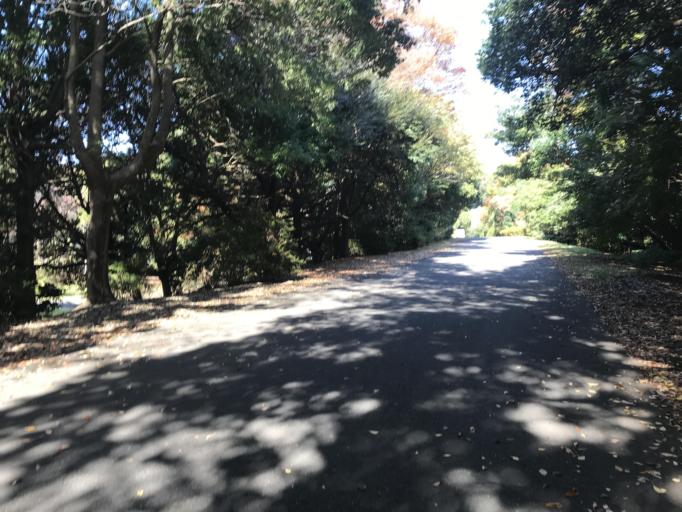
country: JP
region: Tokyo
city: Hino
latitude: 35.7099
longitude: 139.3989
